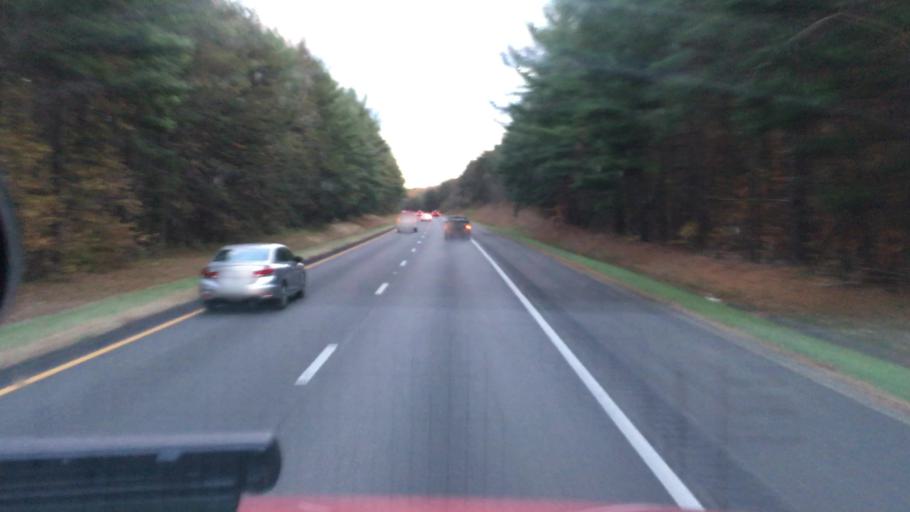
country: US
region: Virginia
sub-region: Fluvanna County
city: Palmyra
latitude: 37.9616
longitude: -78.1760
